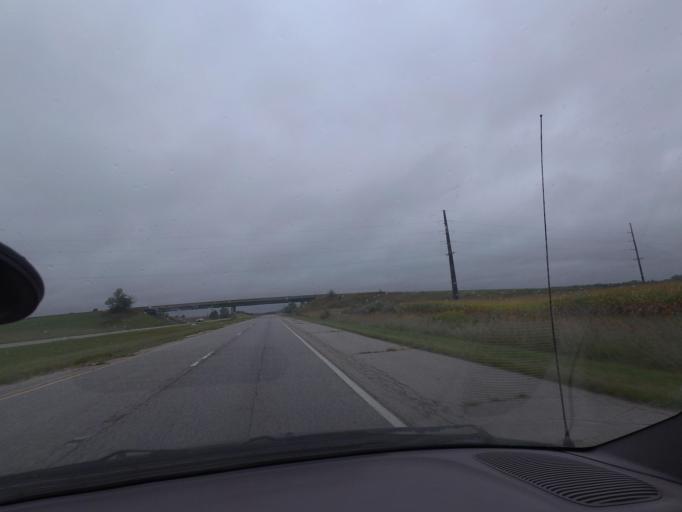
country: US
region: Illinois
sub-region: Pike County
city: Pittsfield
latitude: 39.6712
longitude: -90.8017
